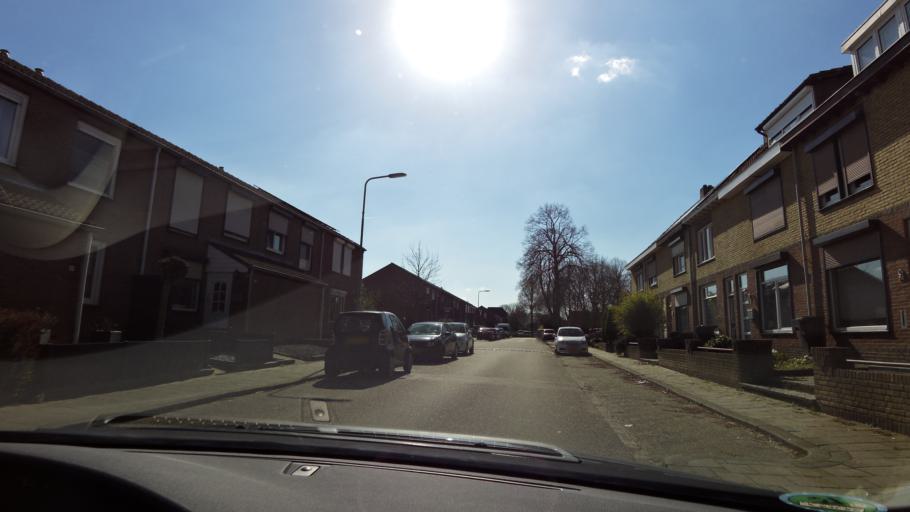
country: NL
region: Limburg
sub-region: Gemeente Sittard-Geleen
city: Sittard
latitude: 50.9881
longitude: 5.8582
